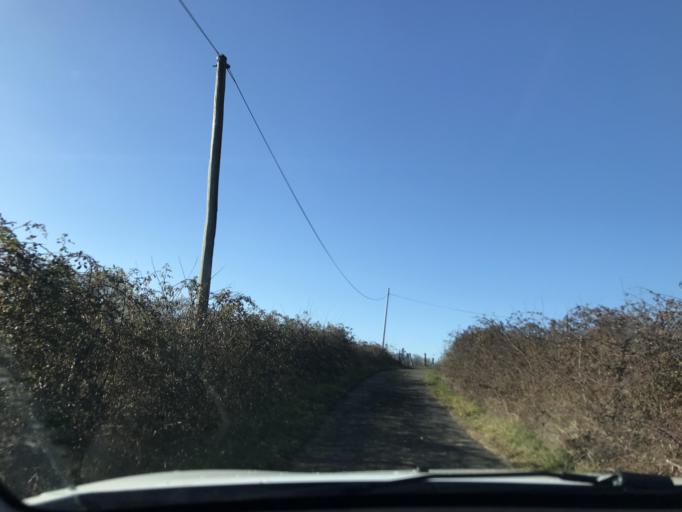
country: FR
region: Poitou-Charentes
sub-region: Departement de la Charente
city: Chasseneuil-sur-Bonnieure
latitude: 45.8359
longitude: 0.5294
